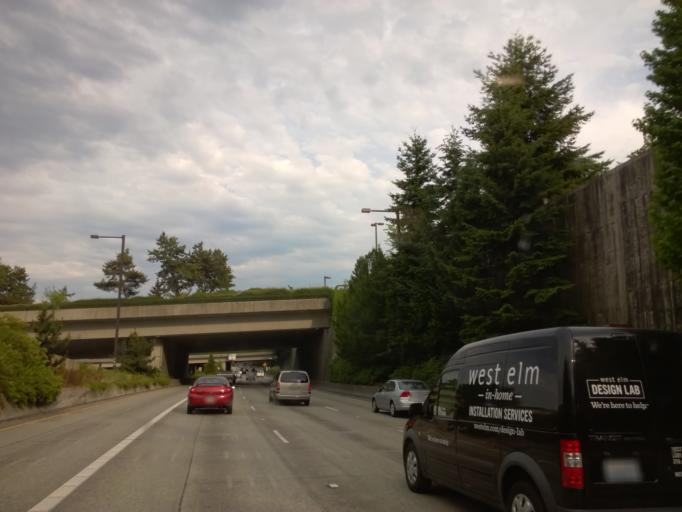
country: US
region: Washington
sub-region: King County
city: Mercer Island
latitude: 47.5865
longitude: -122.2296
